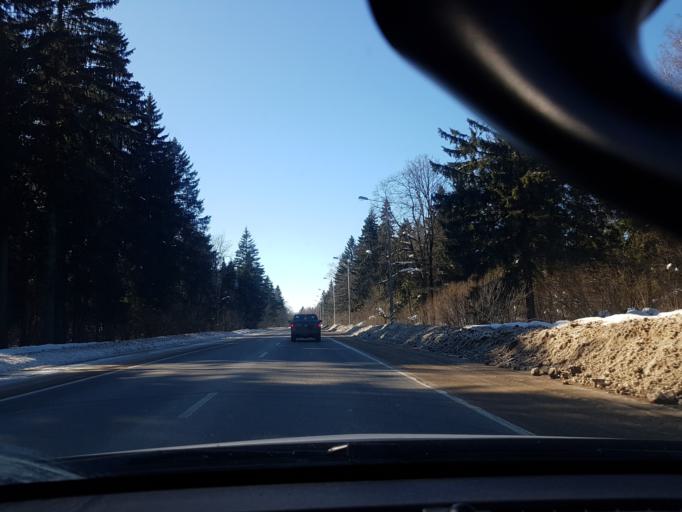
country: RU
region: Moskovskaya
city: Kostrovo
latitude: 55.9133
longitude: 36.7455
